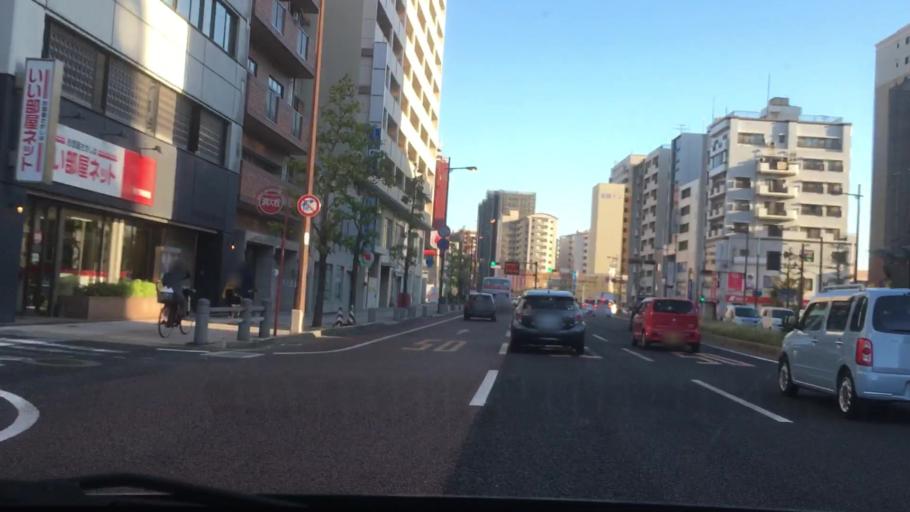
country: JP
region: Nagasaki
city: Sasebo
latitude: 33.1668
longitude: 129.7248
